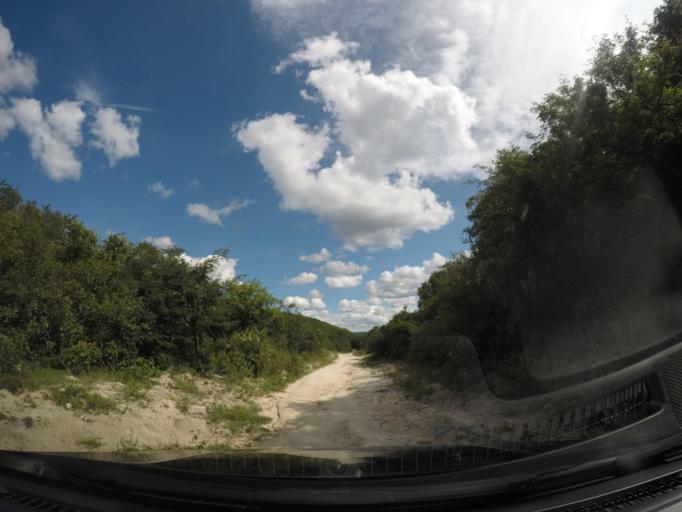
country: BR
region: Bahia
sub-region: Barra Da Estiva
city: Barra da Estiva
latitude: -13.1342
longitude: -41.5942
